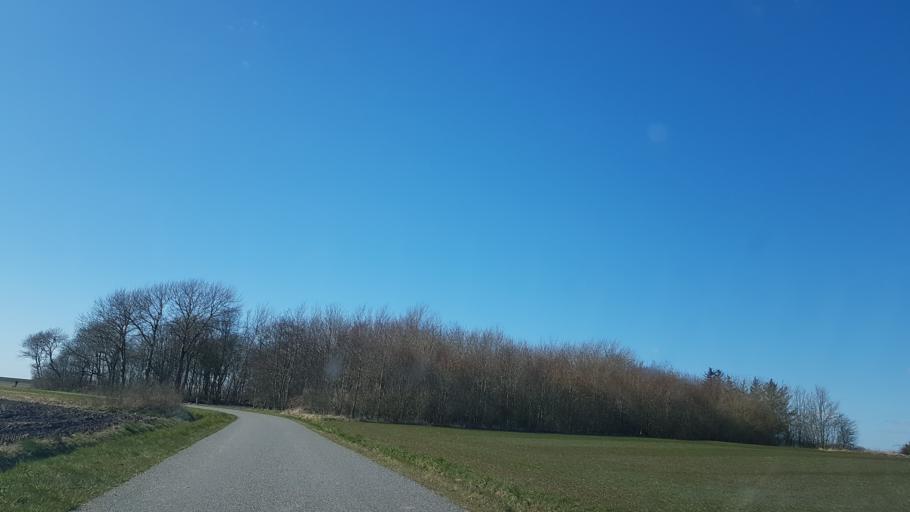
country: DK
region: South Denmark
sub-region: Esbjerg Kommune
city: Ribe
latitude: 55.2569
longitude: 8.6815
